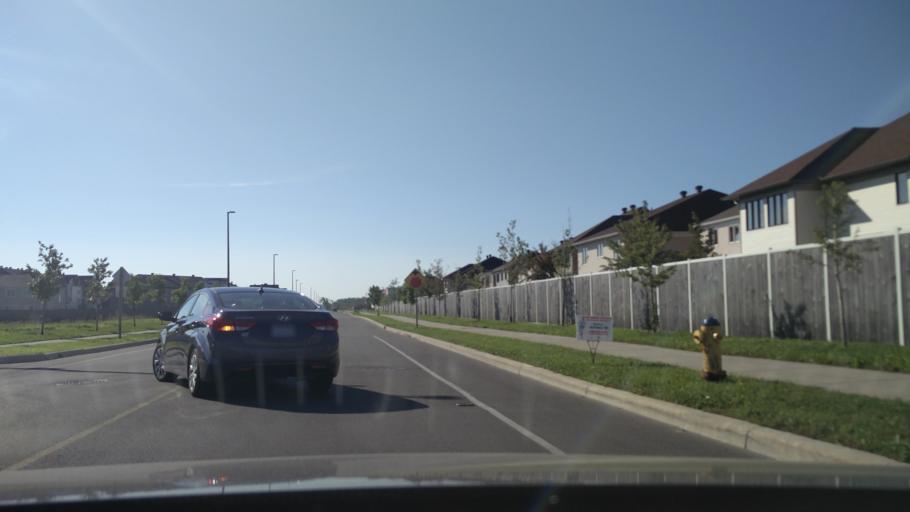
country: CA
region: Ontario
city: Clarence-Rockland
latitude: 45.4538
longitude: -75.4645
